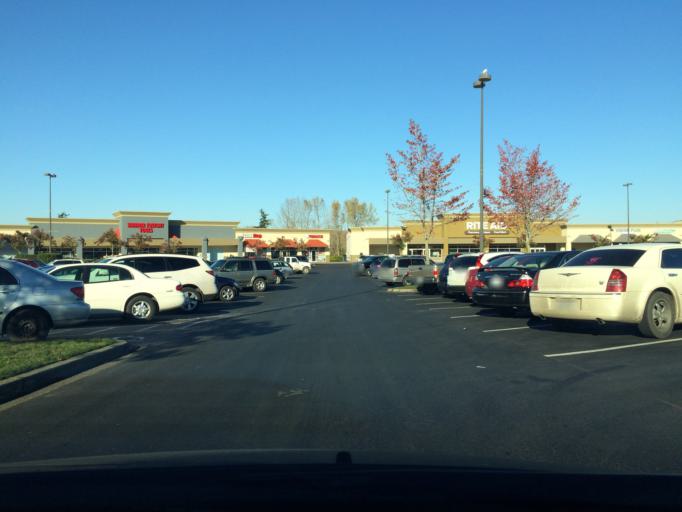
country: US
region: Washington
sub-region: Whatcom County
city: Bellingham
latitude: 48.7734
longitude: -122.4604
